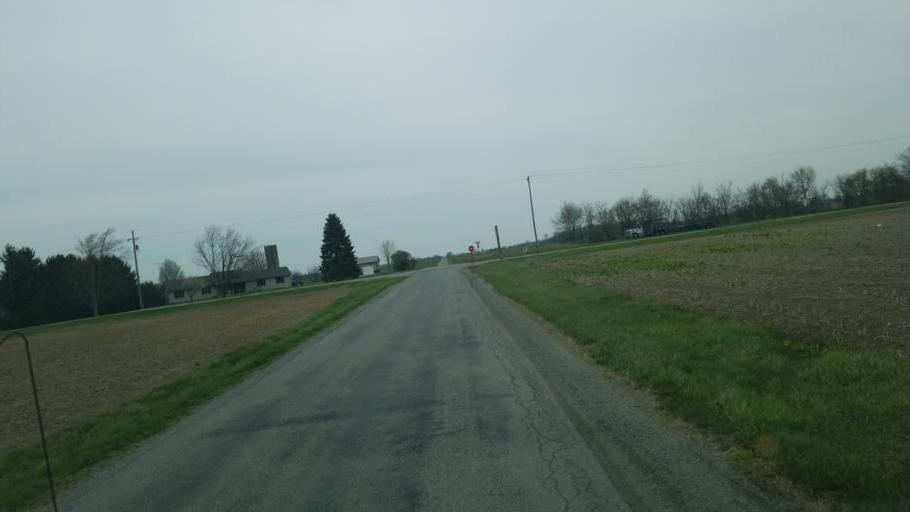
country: US
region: Ohio
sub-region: Hardin County
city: Forest
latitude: 40.9188
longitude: -83.5143
